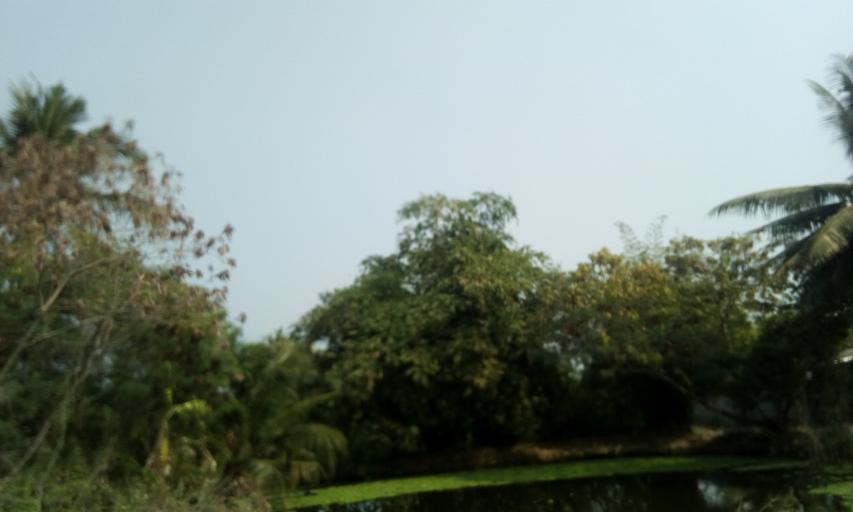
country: TH
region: Pathum Thani
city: Lam Luk Ka
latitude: 13.9544
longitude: 100.7251
